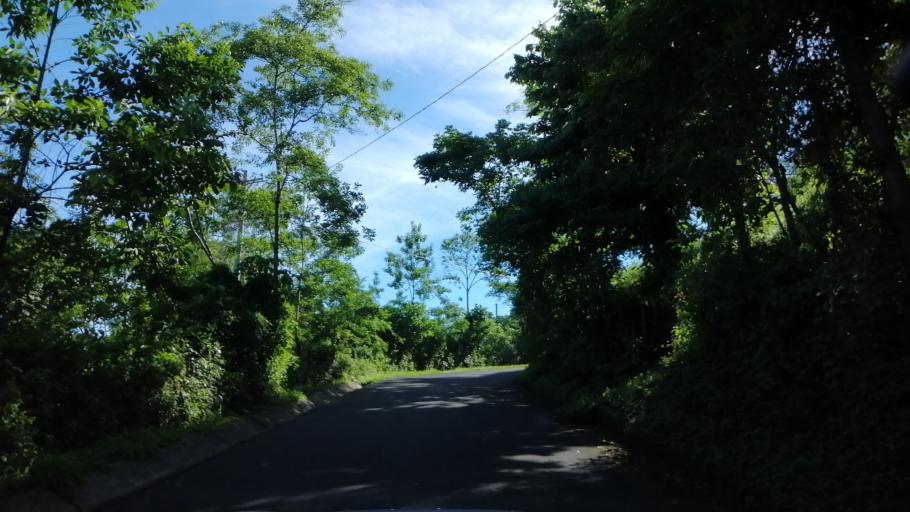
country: SV
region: Morazan
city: Cacaopera
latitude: 13.7882
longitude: -88.0278
